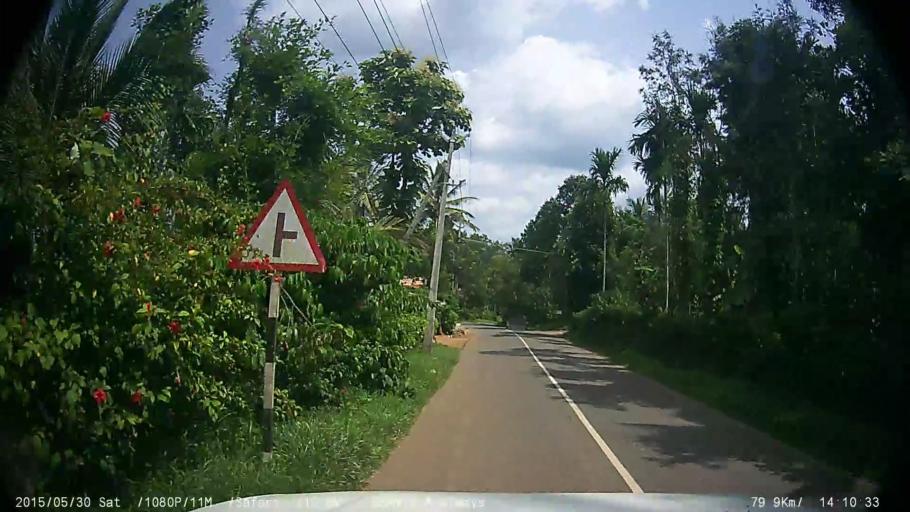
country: IN
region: Kerala
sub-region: Wayanad
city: Panamaram
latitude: 11.7984
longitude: 76.0526
